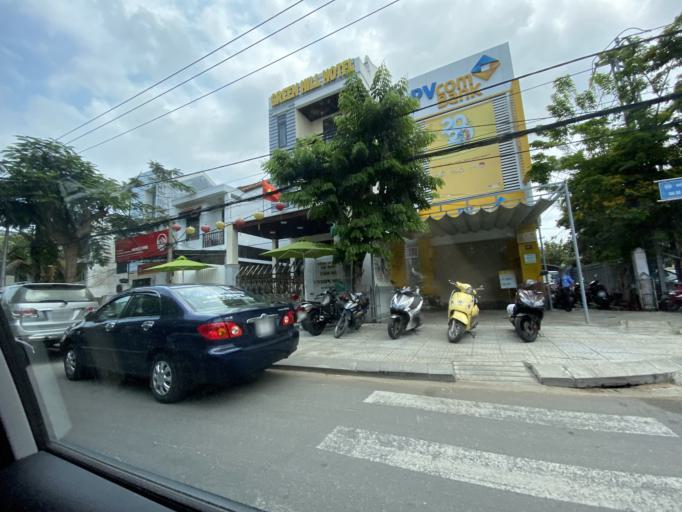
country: VN
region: Quang Nam
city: Hoi An
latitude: 15.8887
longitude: 108.3284
